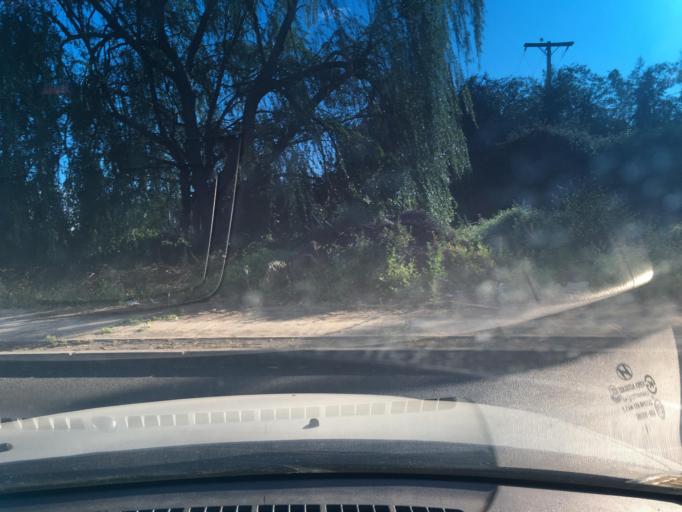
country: CL
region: Santiago Metropolitan
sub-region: Provincia de Chacabuco
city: Chicureo Abajo
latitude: -33.3078
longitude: -70.7180
